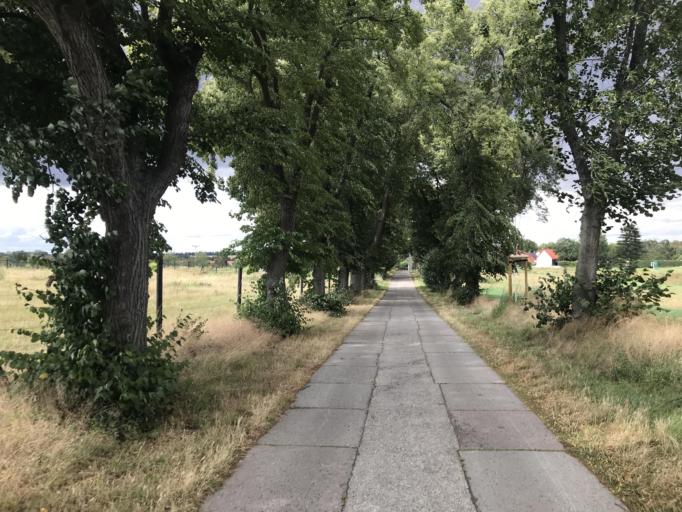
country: DE
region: Saxony-Anhalt
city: Derenburg
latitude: 51.8664
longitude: 10.9172
